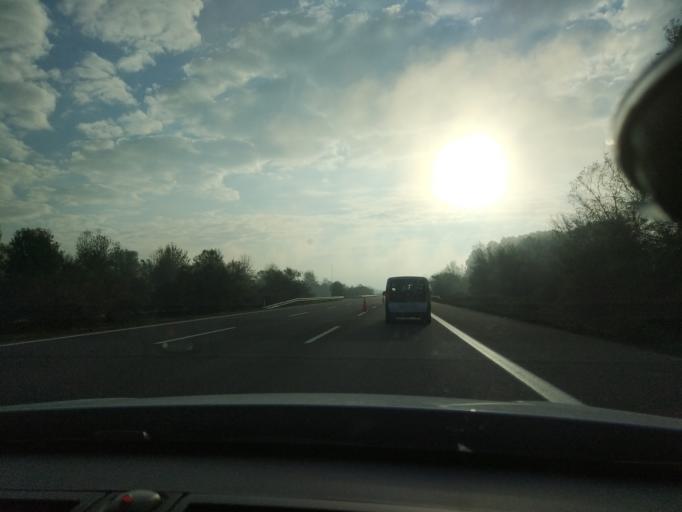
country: TR
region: Duzce
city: Duzce
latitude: 40.8130
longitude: 31.1035
